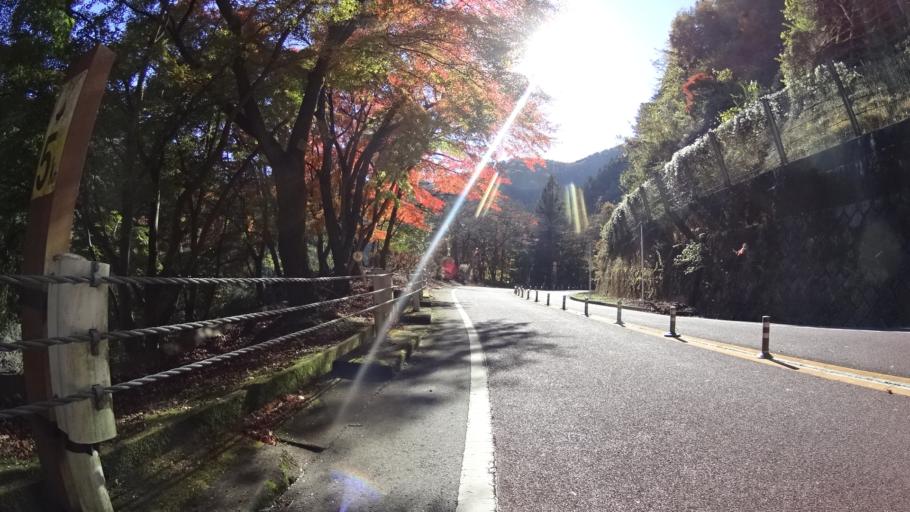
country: JP
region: Yamanashi
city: Uenohara
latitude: 35.7599
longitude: 139.0239
